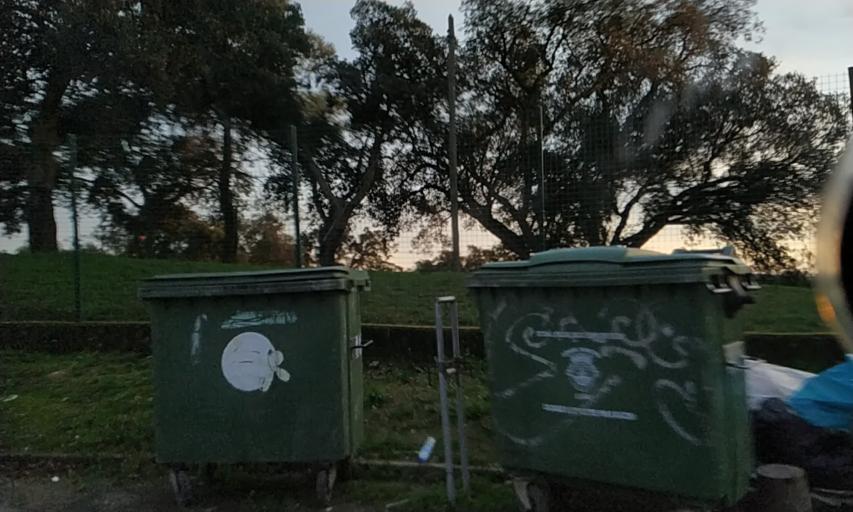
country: PT
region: Setubal
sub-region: Setubal
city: Setubal
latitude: 38.5213
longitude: -8.8369
